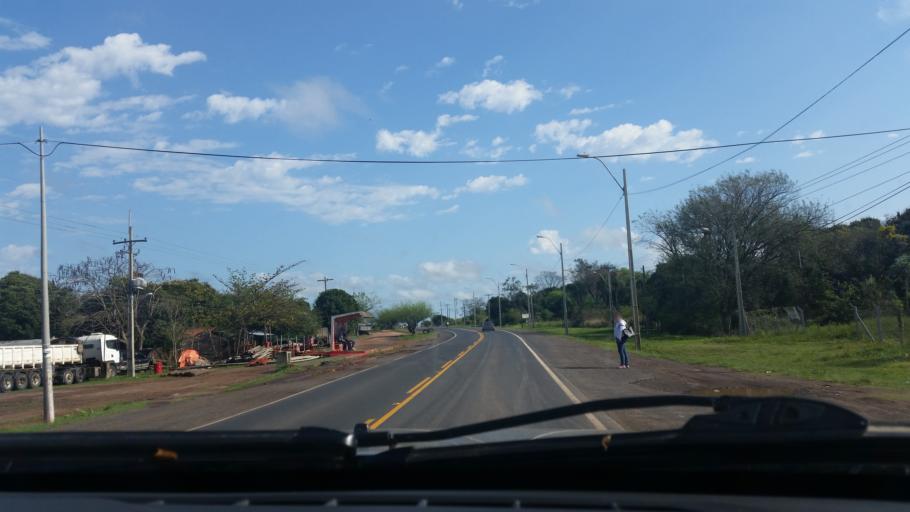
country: PY
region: Presidente Hayes
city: Benjamin Aceval
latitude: -25.0270
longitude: -57.5546
